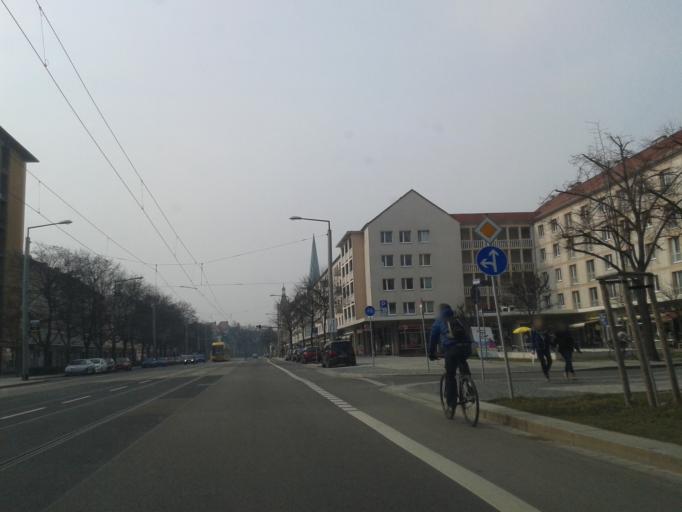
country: DE
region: Saxony
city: Albertstadt
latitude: 51.0442
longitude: 13.7802
